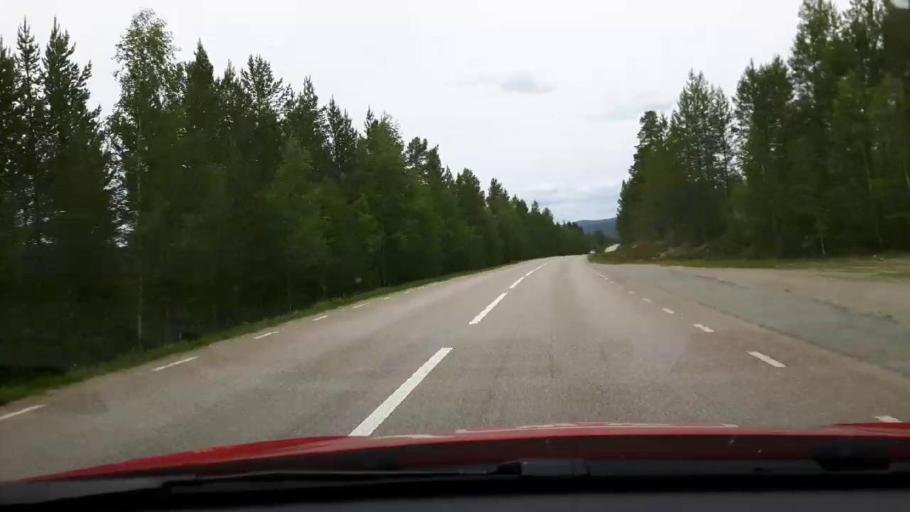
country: SE
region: Jaemtland
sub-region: Harjedalens Kommun
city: Sveg
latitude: 62.2457
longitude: 13.8439
